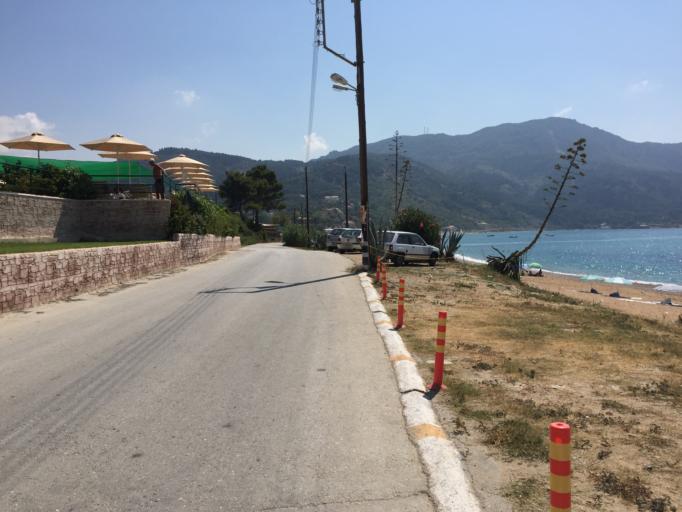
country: GR
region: Ionian Islands
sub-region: Nomos Kerkyras
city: Agios Georgis
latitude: 39.7197
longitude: 19.6759
